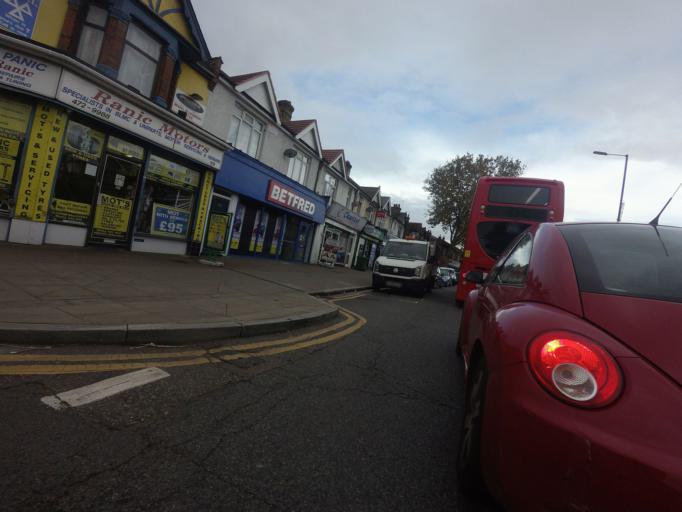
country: GB
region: England
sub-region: Greater London
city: East Ham
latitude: 51.5266
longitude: 0.0564
